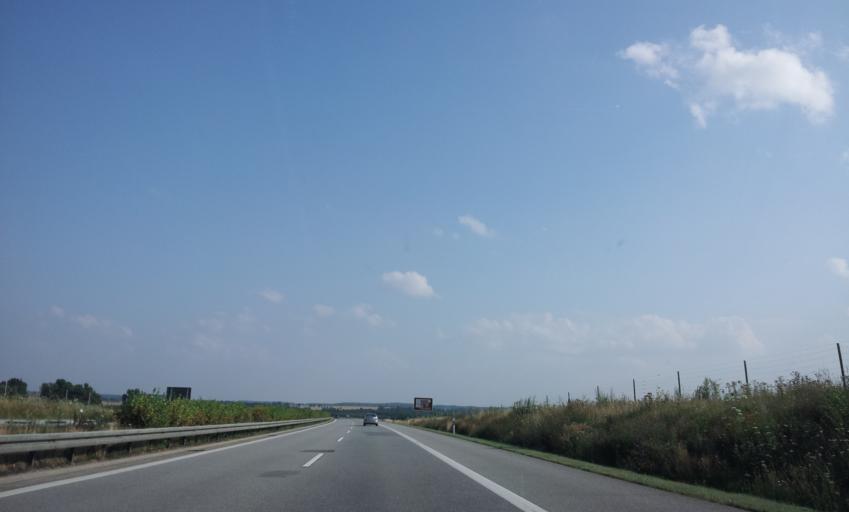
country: DE
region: Mecklenburg-Vorpommern
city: Kessin
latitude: 53.6875
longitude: 13.3273
